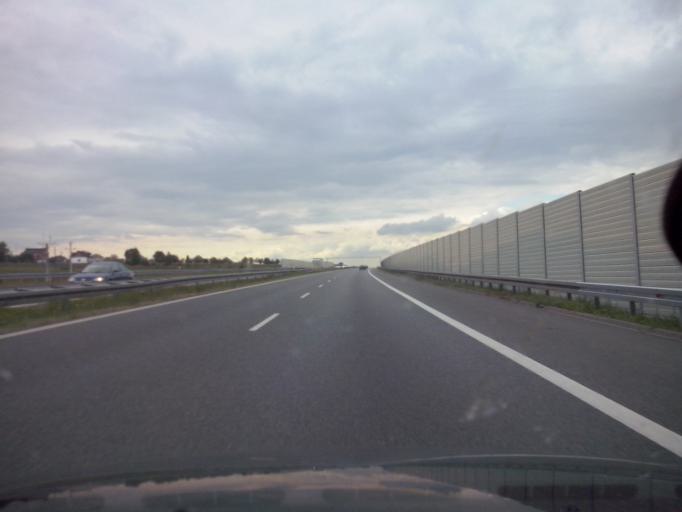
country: PL
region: Lesser Poland Voivodeship
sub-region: Powiat wielicki
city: Szarow
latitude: 49.9911
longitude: 20.2363
